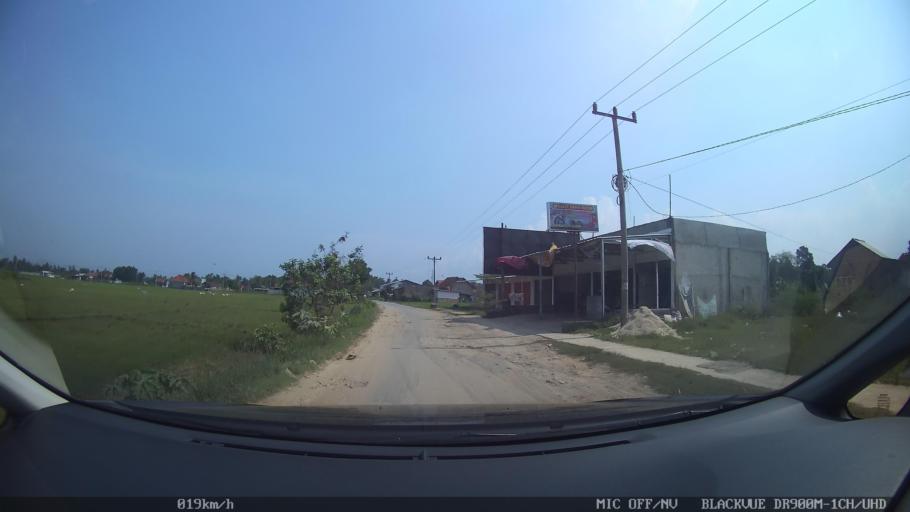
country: ID
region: Lampung
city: Natar
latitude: -5.3036
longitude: 105.2238
